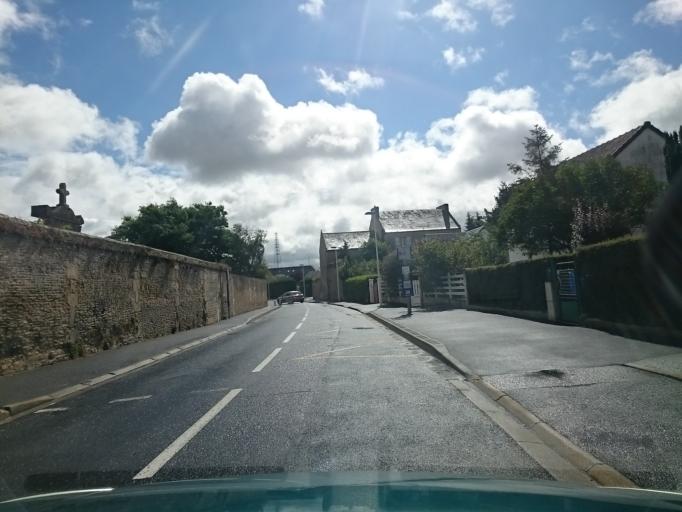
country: FR
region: Lower Normandy
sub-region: Departement du Calvados
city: Ifs
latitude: 49.1394
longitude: -0.3483
